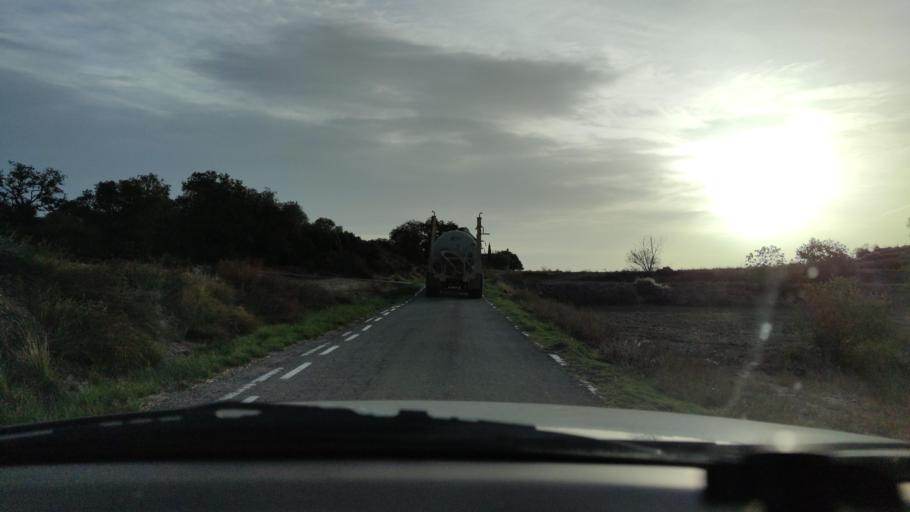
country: ES
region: Catalonia
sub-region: Provincia de Lleida
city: Agramunt
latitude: 41.8376
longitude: 1.0937
